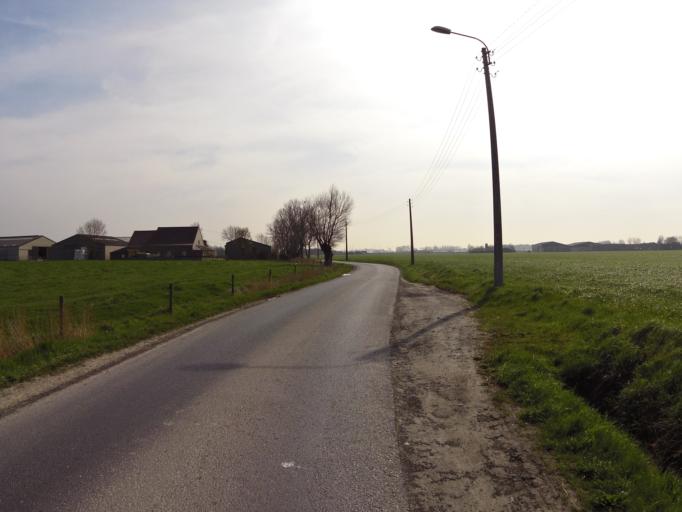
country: BE
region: Flanders
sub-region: Provincie West-Vlaanderen
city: Oudenburg
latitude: 51.1768
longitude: 2.9850
